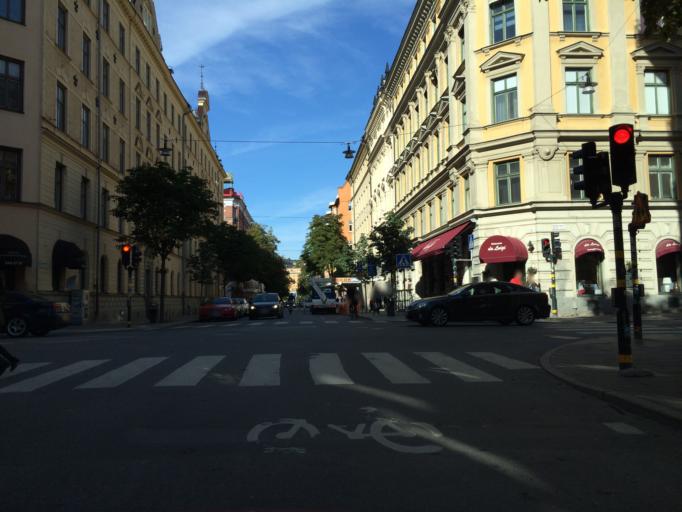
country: SE
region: Stockholm
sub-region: Stockholms Kommun
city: Stockholm
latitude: 59.3152
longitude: 18.0643
